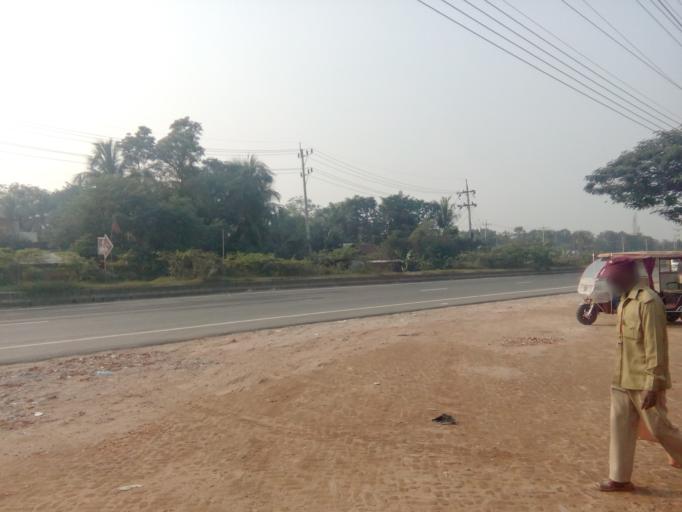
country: BD
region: Chittagong
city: Comilla
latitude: 23.4433
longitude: 91.1498
